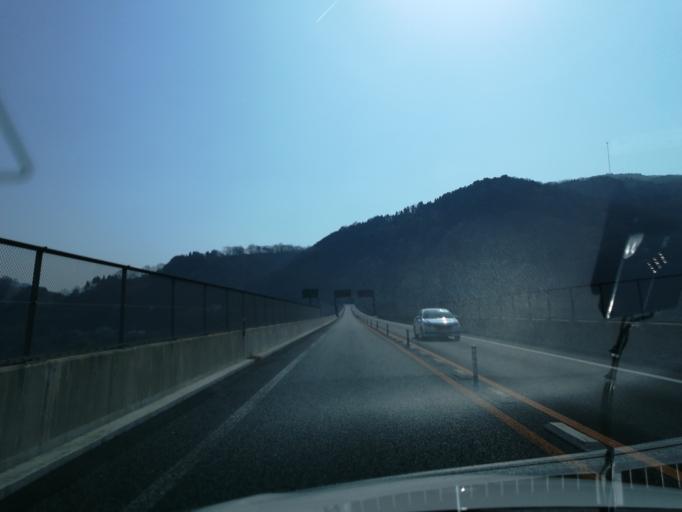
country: JP
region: Tokushima
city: Ikedacho
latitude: 34.0249
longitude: 133.7835
